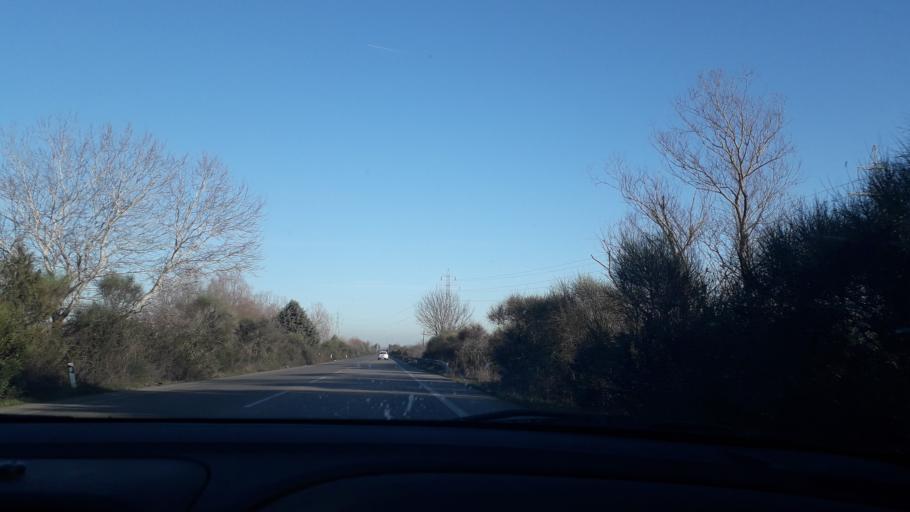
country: GR
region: Central Macedonia
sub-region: Nomos Pellis
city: Melissi
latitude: 40.7779
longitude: 22.3444
